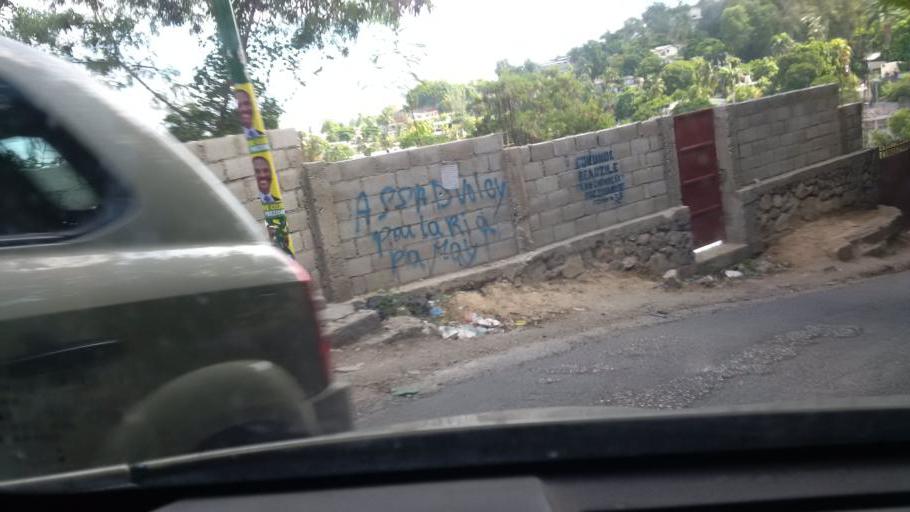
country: HT
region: Ouest
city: Delmas 73
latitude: 18.5400
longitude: -72.3176
